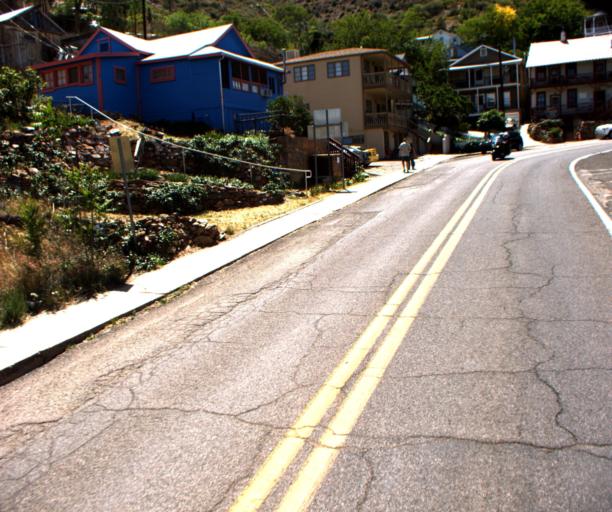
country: US
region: Arizona
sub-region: Yavapai County
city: Clarkdale
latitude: 34.7490
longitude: -112.1137
